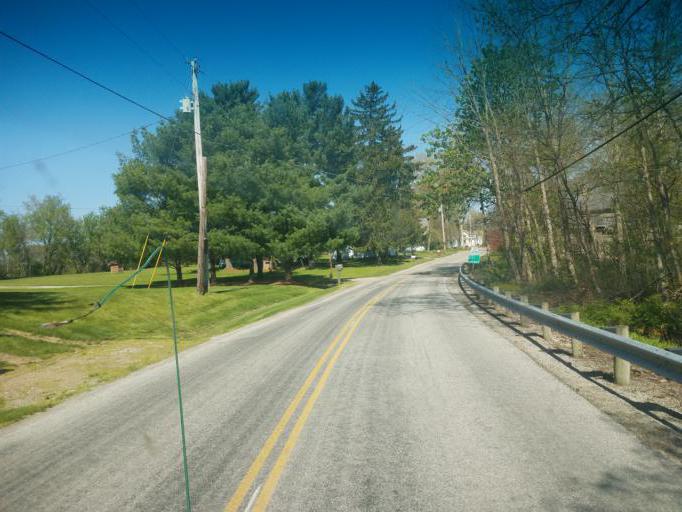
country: US
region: Ohio
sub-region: Medina County
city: Lodi
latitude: 40.9889
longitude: -82.0014
